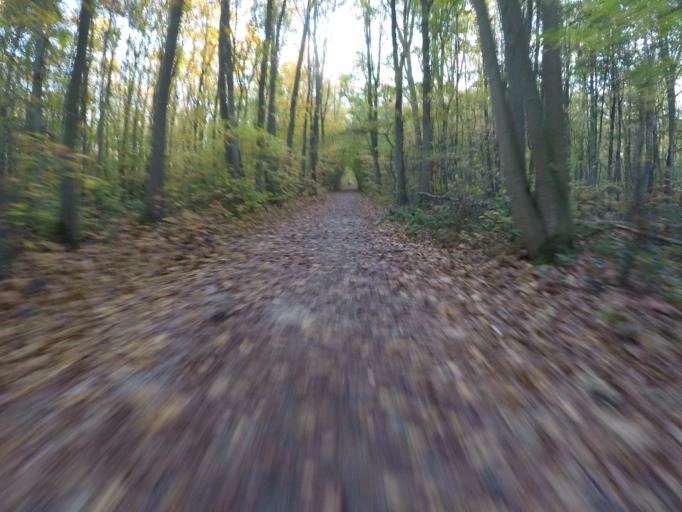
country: BE
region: Flanders
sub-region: Provincie Vlaams-Brabant
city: Begijnendijk
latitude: 51.0261
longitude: 4.7808
